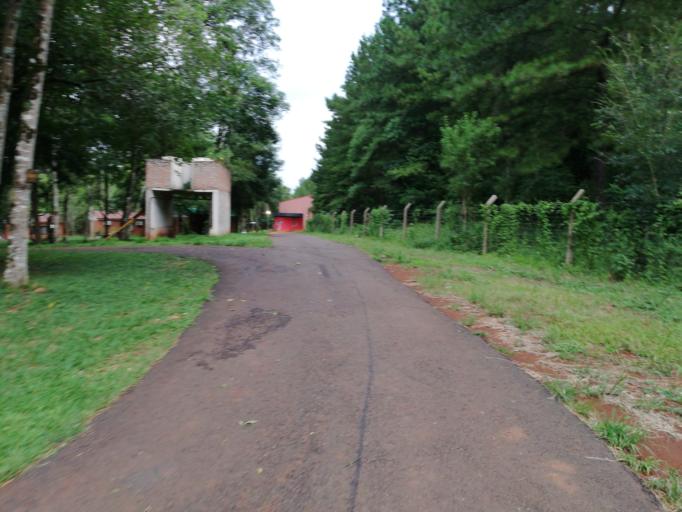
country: AR
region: Misiones
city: Puerto Leoni
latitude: -26.9994
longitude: -55.1805
